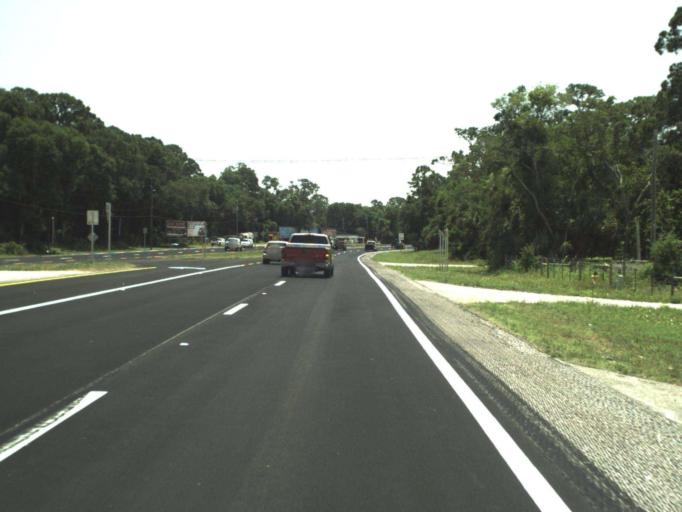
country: US
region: Florida
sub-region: Volusia County
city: Ponce Inlet
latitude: 29.1023
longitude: -80.9715
